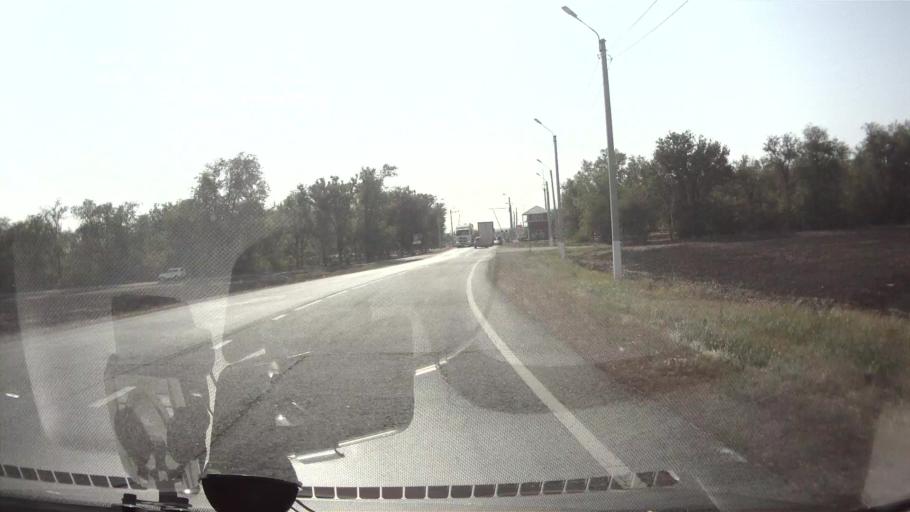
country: RU
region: Krasnodarskiy
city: Belaya Glina
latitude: 46.1006
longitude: 40.8529
